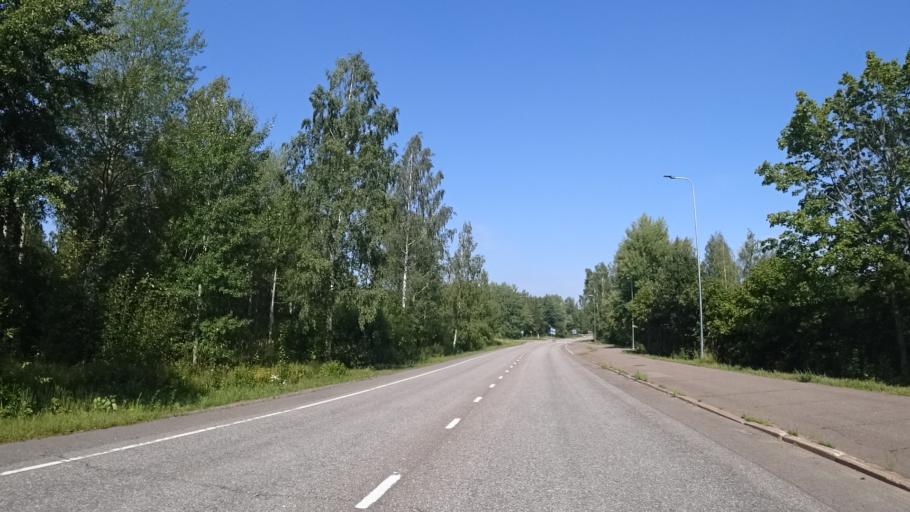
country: FI
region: Kymenlaakso
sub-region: Kotka-Hamina
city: Karhula
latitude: 60.5098
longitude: 26.9460
